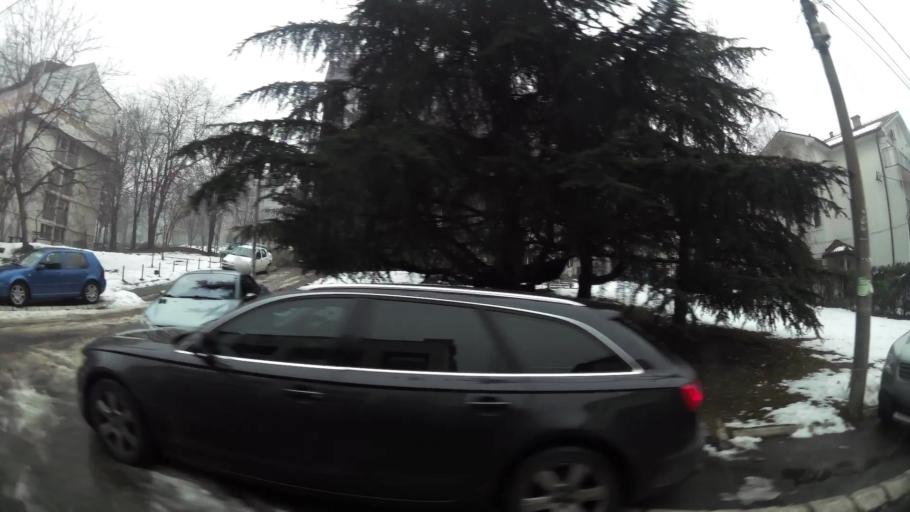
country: RS
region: Central Serbia
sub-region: Belgrade
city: Cukarica
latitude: 44.7757
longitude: 20.4182
